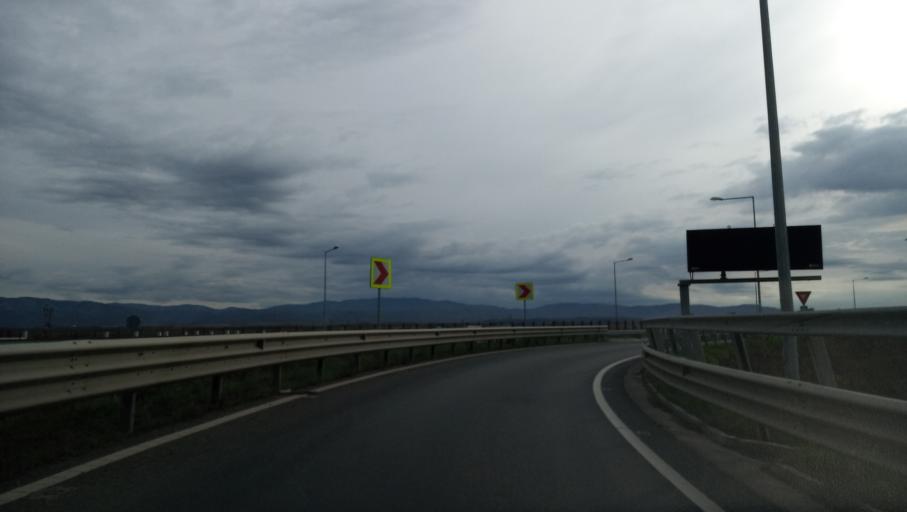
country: RO
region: Timis
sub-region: Comuna Margina
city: Margina
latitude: 45.8599
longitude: 22.2458
